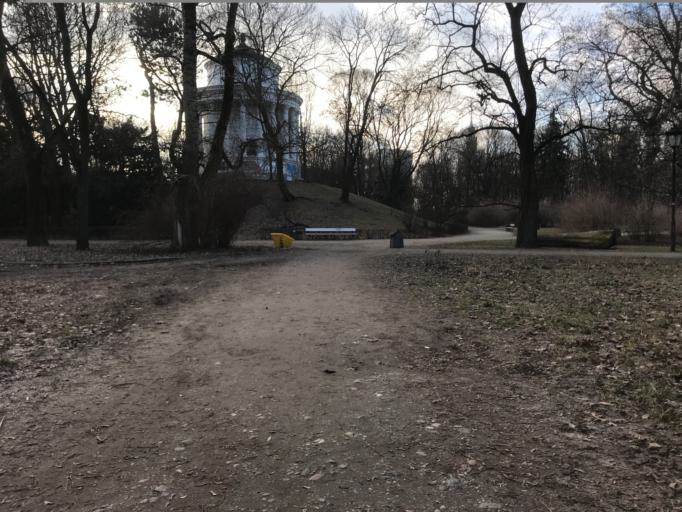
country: PL
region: Masovian Voivodeship
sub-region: Warszawa
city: Warsaw
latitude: 52.2419
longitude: 21.0069
